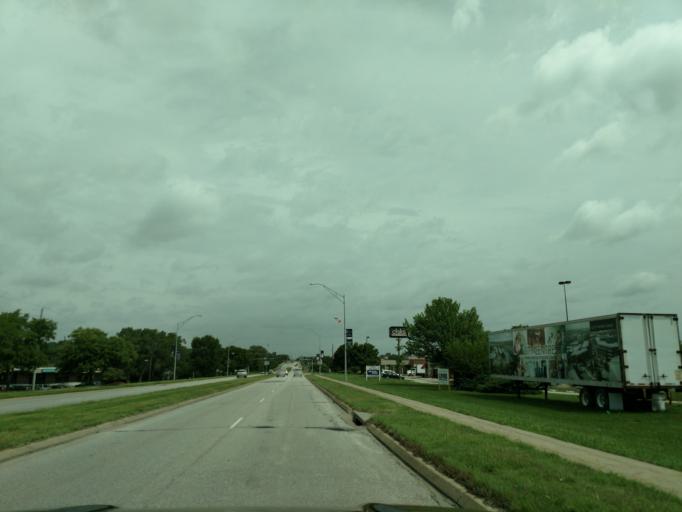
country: US
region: Nebraska
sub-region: Sarpy County
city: La Vista
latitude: 41.1812
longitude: -96.0429
